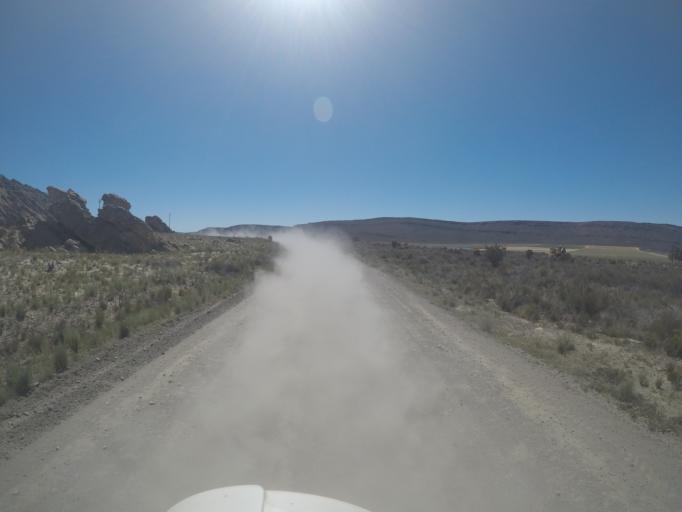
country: ZA
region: Western Cape
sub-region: Cape Winelands District Municipality
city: Ceres
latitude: -32.8438
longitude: 19.4483
